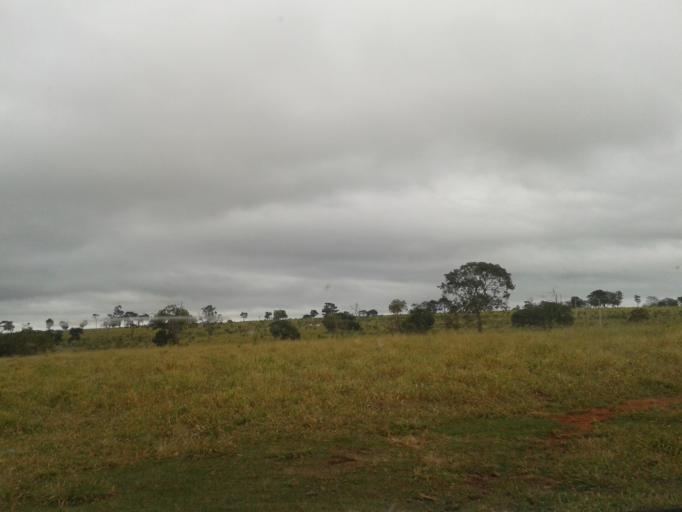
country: BR
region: Minas Gerais
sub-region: Campina Verde
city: Campina Verde
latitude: -19.4095
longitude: -49.6444
